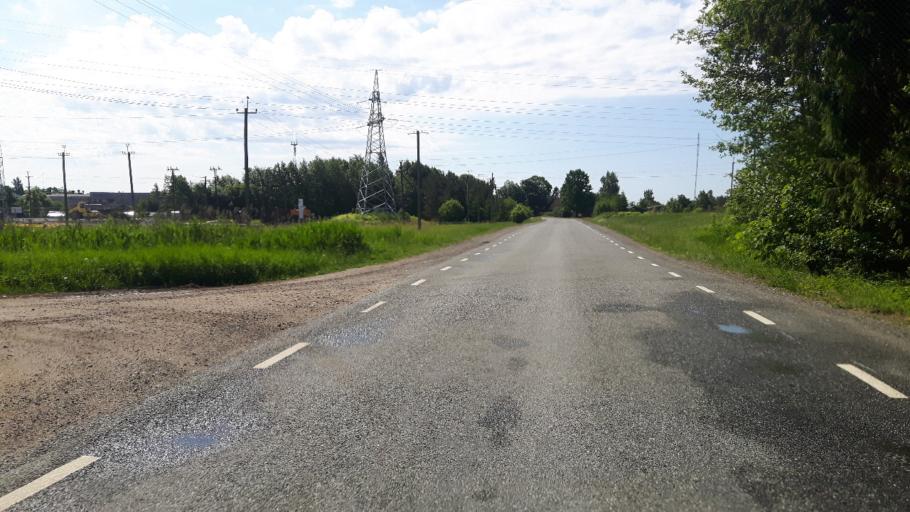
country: EE
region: Paernumaa
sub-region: Vaendra vald (alev)
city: Vandra
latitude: 58.6592
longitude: 25.0237
